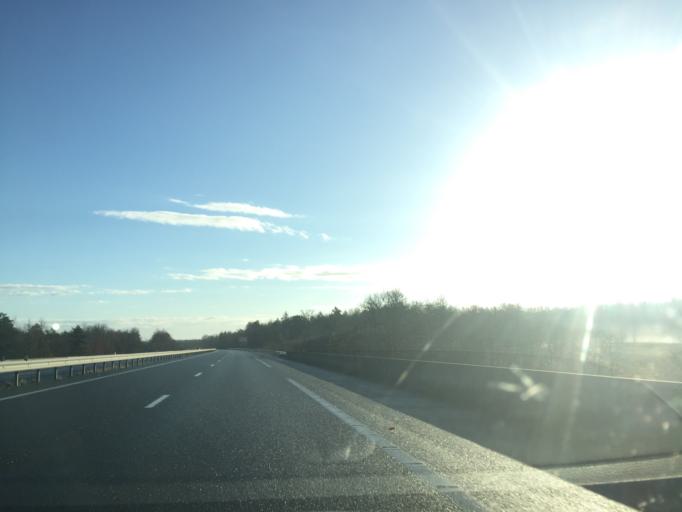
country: FR
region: Aquitaine
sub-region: Departement de la Dordogne
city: Thenon
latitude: 45.1767
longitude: 0.9882
